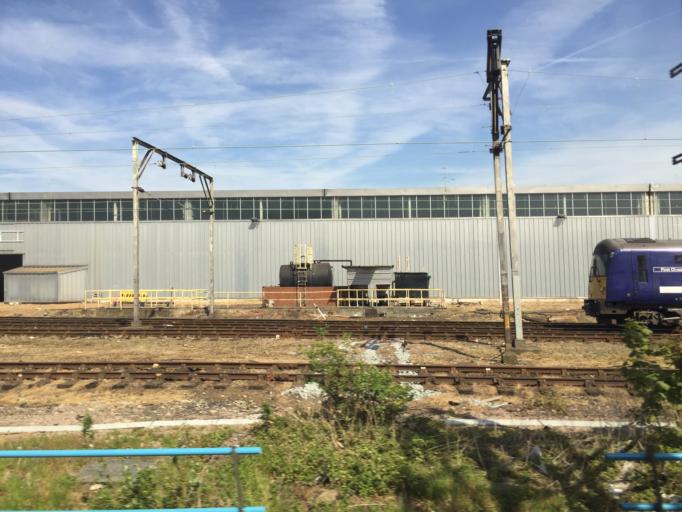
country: GB
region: England
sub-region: Greater London
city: Ilford
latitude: 51.5631
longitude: 0.0893
